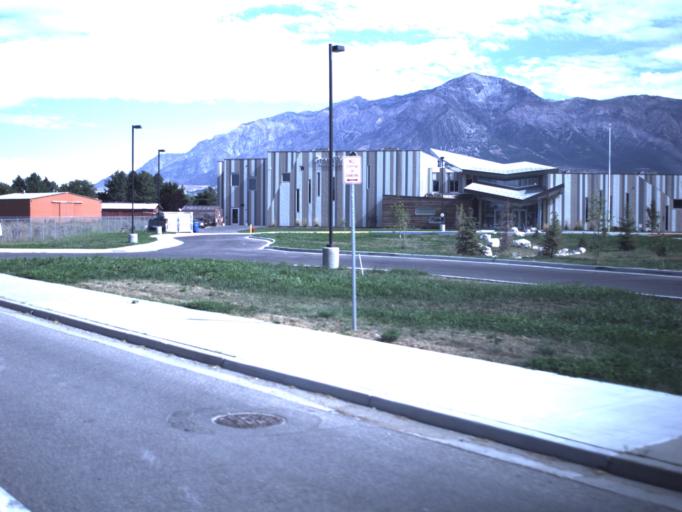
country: US
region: Utah
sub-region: Weber County
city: Harrisville
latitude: 41.2734
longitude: -111.9800
